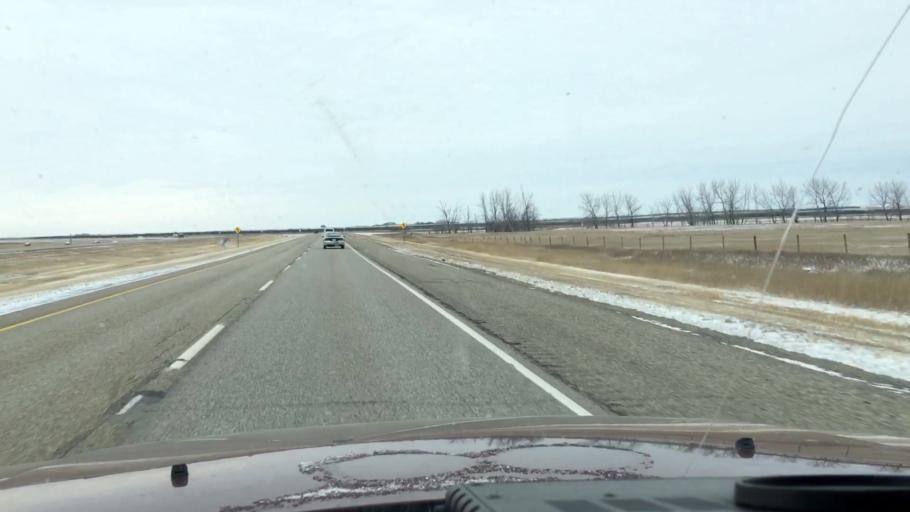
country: CA
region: Saskatchewan
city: Saskatoon
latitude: 51.4792
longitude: -106.2501
